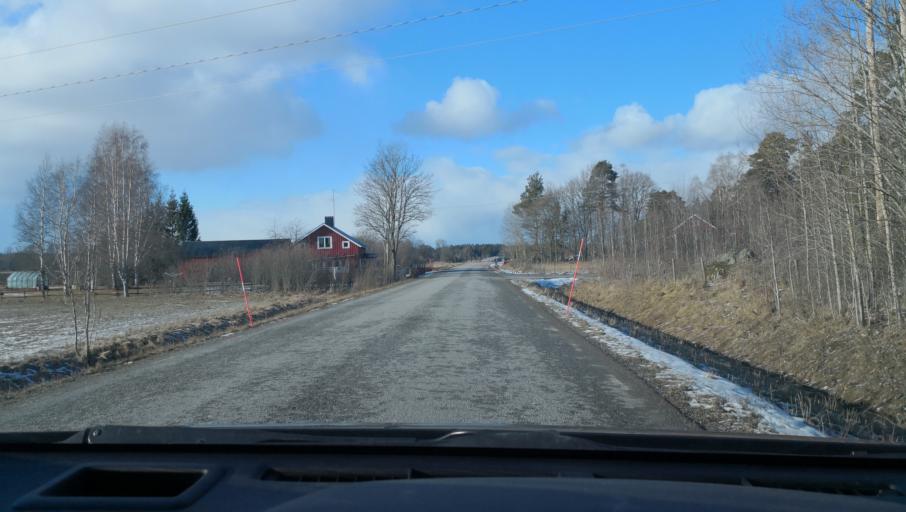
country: SE
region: Uppsala
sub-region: Enkopings Kommun
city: Hummelsta
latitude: 59.6368
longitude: 16.9709
